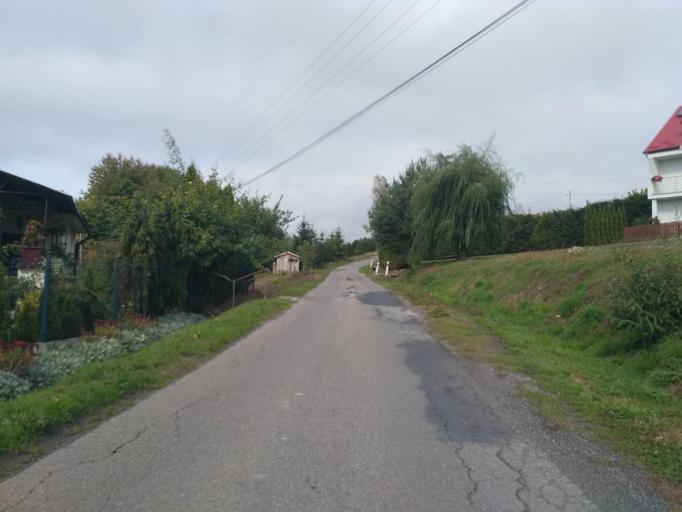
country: PL
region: Subcarpathian Voivodeship
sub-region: Powiat debicki
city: Brzostek
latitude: 49.9550
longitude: 21.4404
